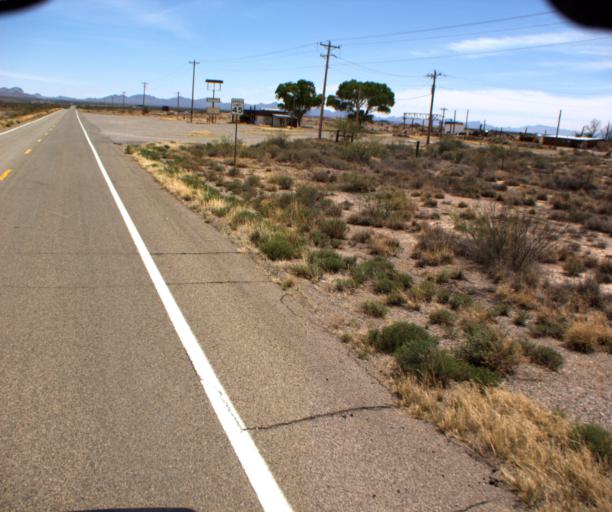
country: US
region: New Mexico
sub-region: Hidalgo County
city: Lordsburg
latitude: 32.2649
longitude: -109.2200
